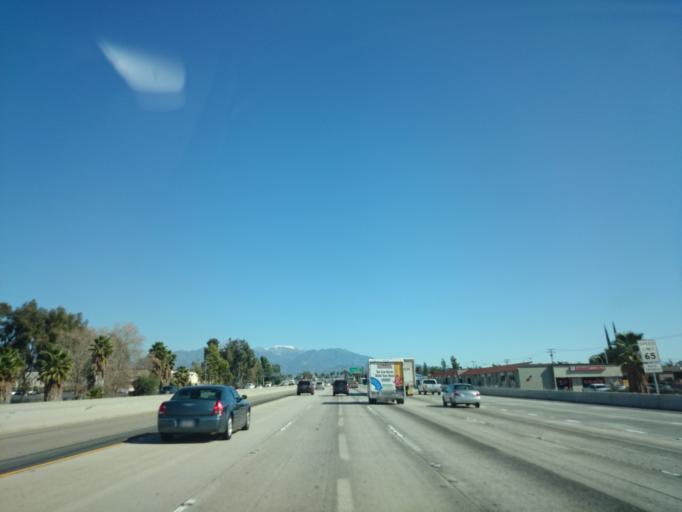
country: US
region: California
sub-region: San Bernardino County
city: Loma Linda
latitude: 34.0637
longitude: -117.2704
